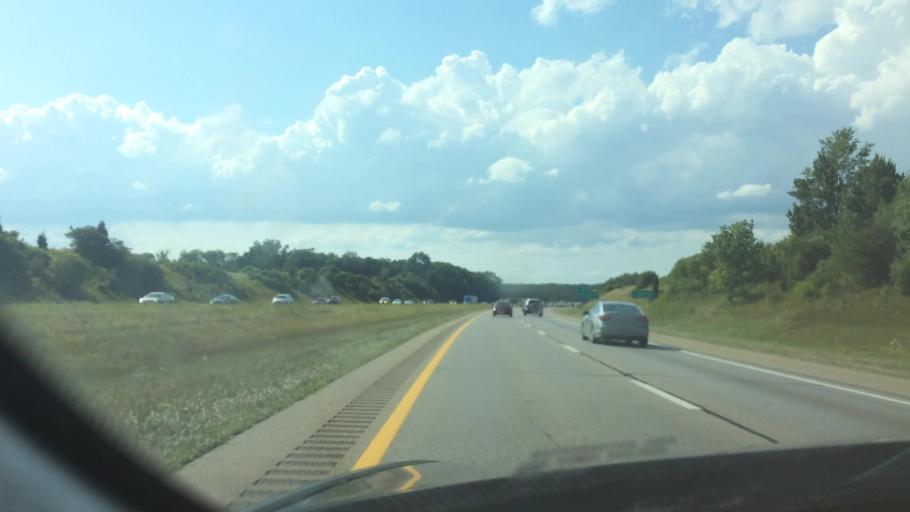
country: US
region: Ohio
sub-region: Lucas County
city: Maumee
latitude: 41.5377
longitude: -83.6751
